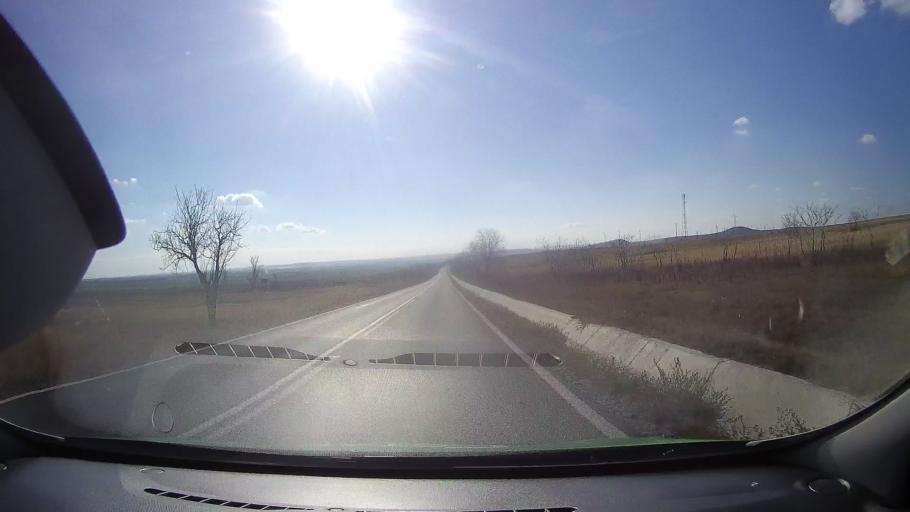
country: RO
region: Tulcea
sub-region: Comuna Ceamurlia de Jos
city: Ceamurlia de Jos
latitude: 44.8129
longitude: 28.6915
